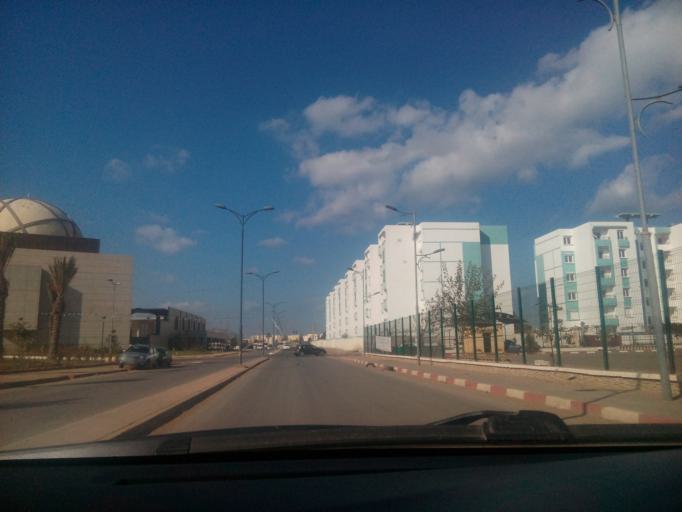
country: DZ
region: Oran
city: Es Senia
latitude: 35.6788
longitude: -0.5999
